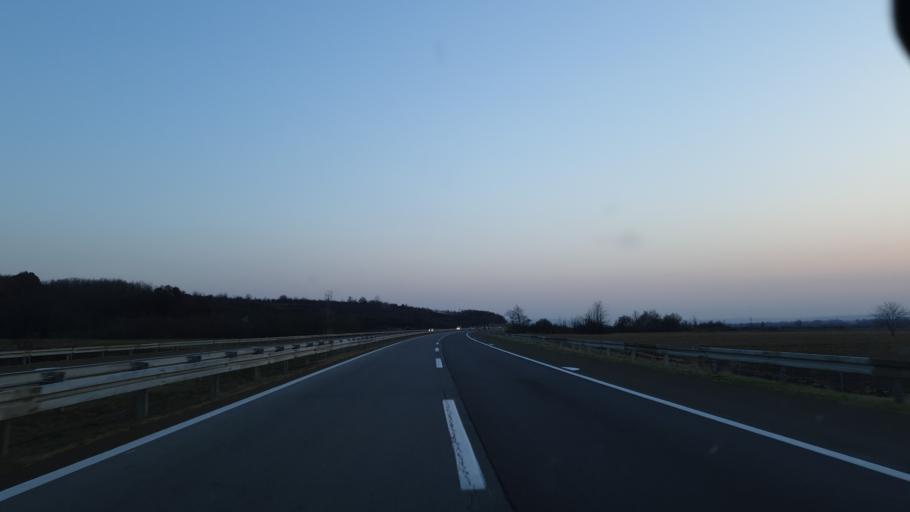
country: RS
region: Central Serbia
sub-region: Pomoravski Okrug
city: Paracin
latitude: 43.8282
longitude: 21.4288
